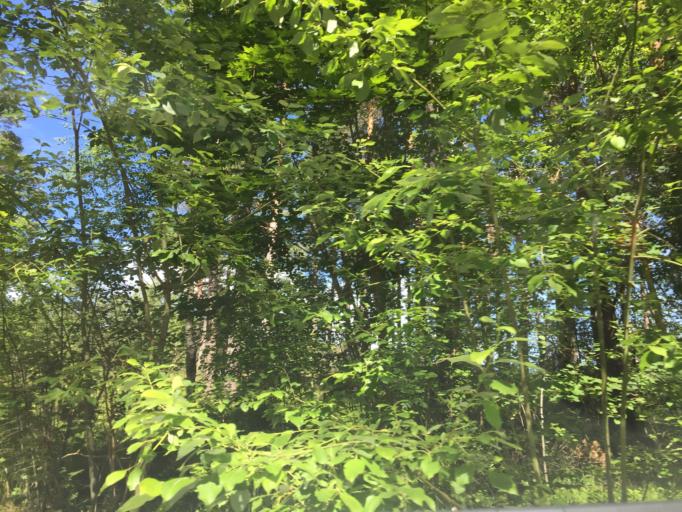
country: LV
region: Rojas
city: Roja
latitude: 57.5064
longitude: 22.7897
